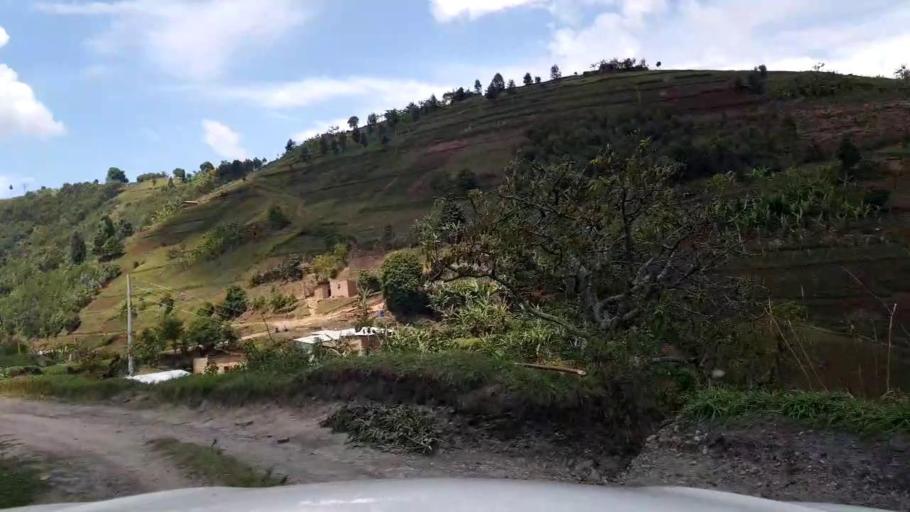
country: RW
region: Northern Province
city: Byumba
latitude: -1.5274
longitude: 30.1305
